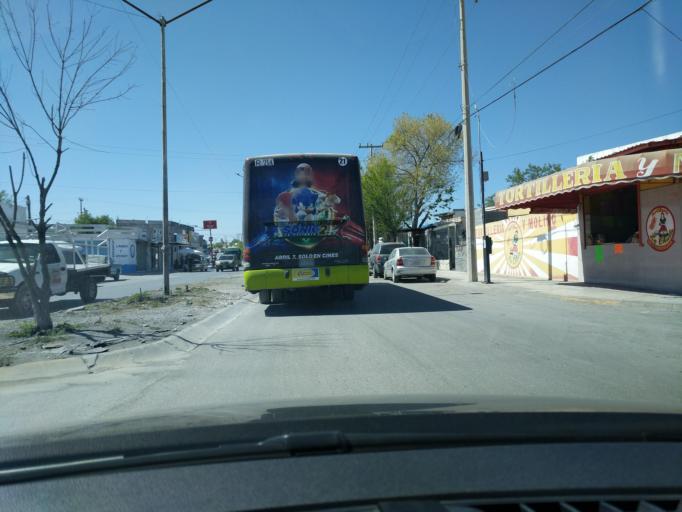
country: MX
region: Nuevo Leon
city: Juarez
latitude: 25.6516
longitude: -100.0752
